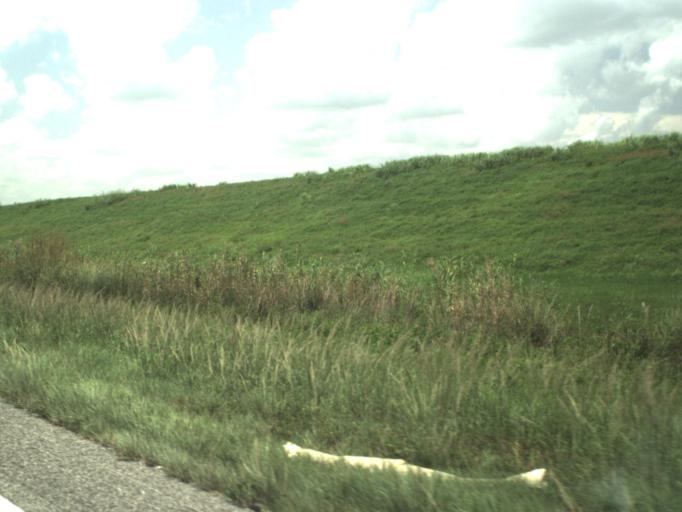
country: US
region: Florida
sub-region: Hendry County
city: Clewiston
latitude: 26.7417
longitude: -80.8814
